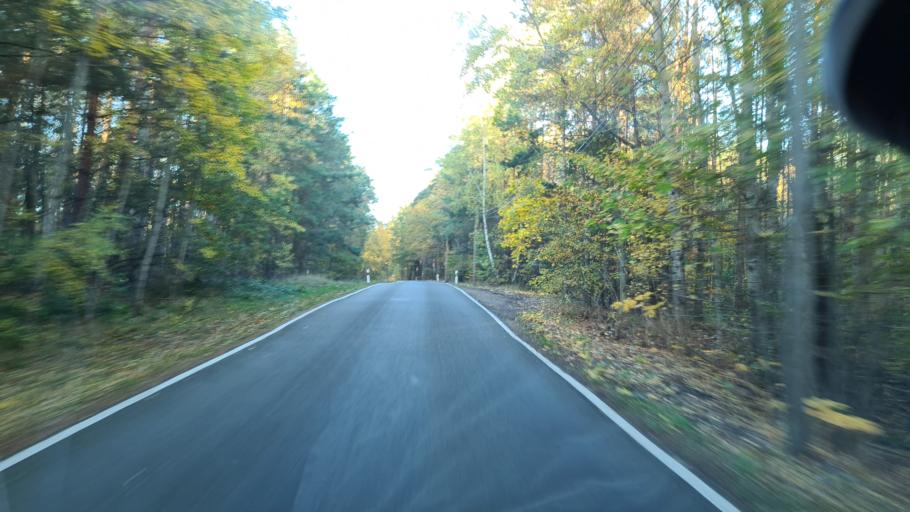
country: DE
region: Saxony
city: Dahlen
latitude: 51.3922
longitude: 13.0198
